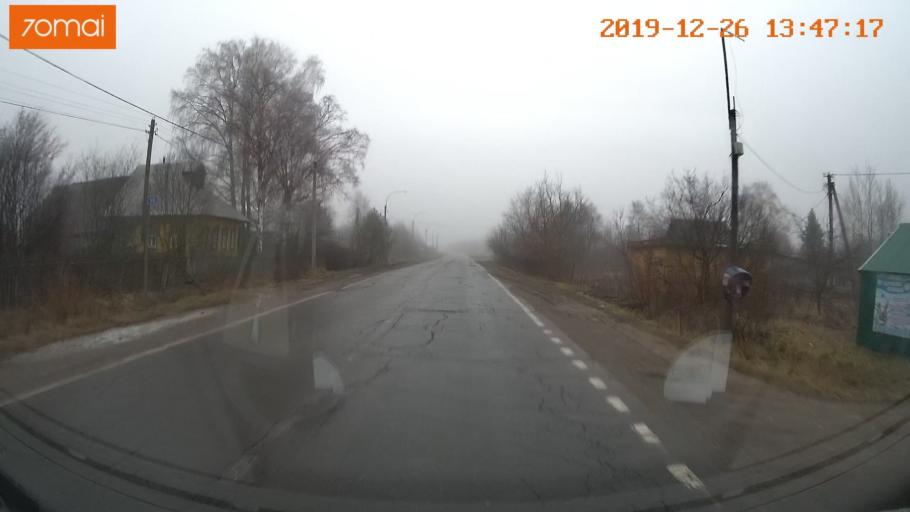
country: RU
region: Vologda
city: Sheksna
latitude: 58.6859
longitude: 38.5327
